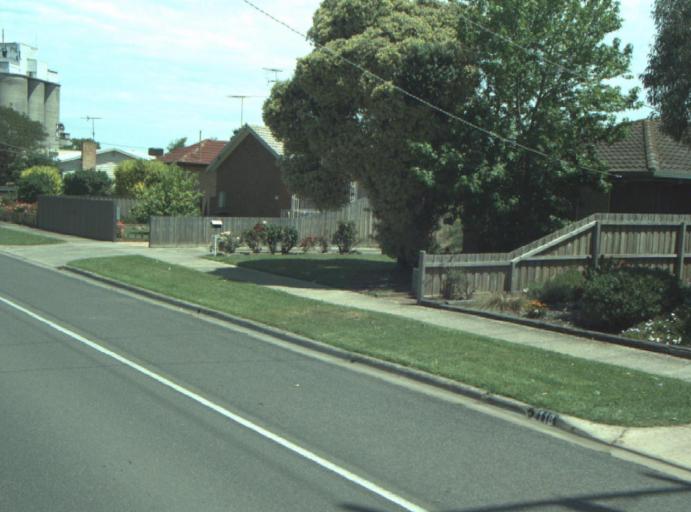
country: AU
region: Victoria
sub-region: Greater Geelong
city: Hamlyn Heights
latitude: -38.1358
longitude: 144.3189
